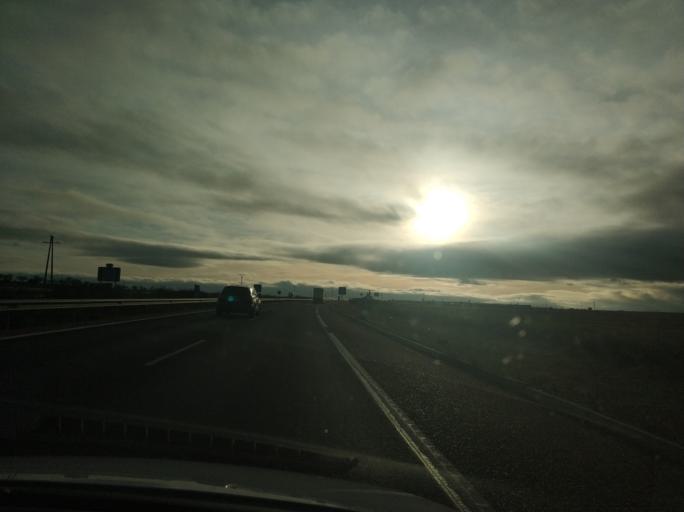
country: ES
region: Castille and Leon
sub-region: Provincia de Valladolid
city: Siete Iglesias de Trabancos
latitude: 41.3269
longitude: -5.1953
